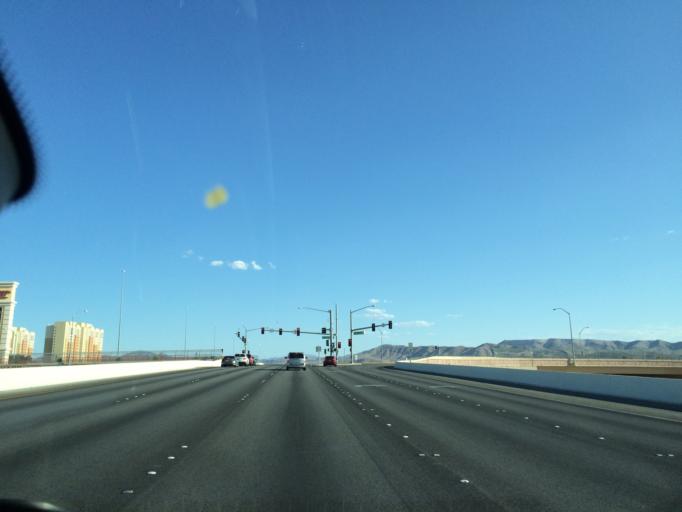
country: US
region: Nevada
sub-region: Clark County
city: Enterprise
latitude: 36.0143
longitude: -115.1811
